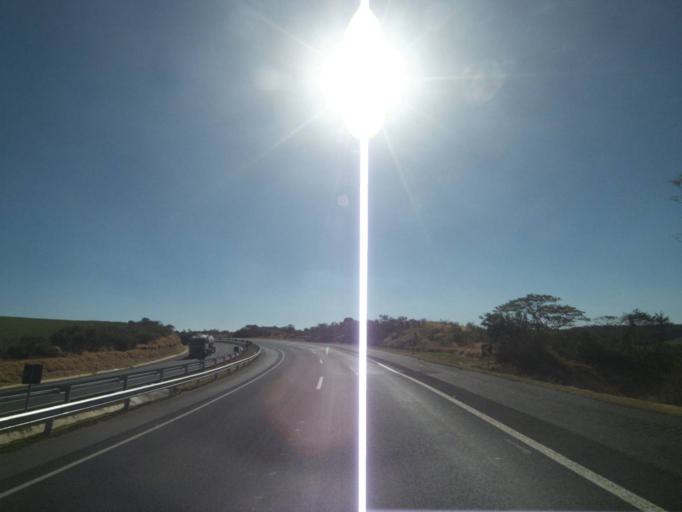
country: BR
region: Parana
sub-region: Tibagi
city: Tibagi
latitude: -24.8509
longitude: -50.4617
